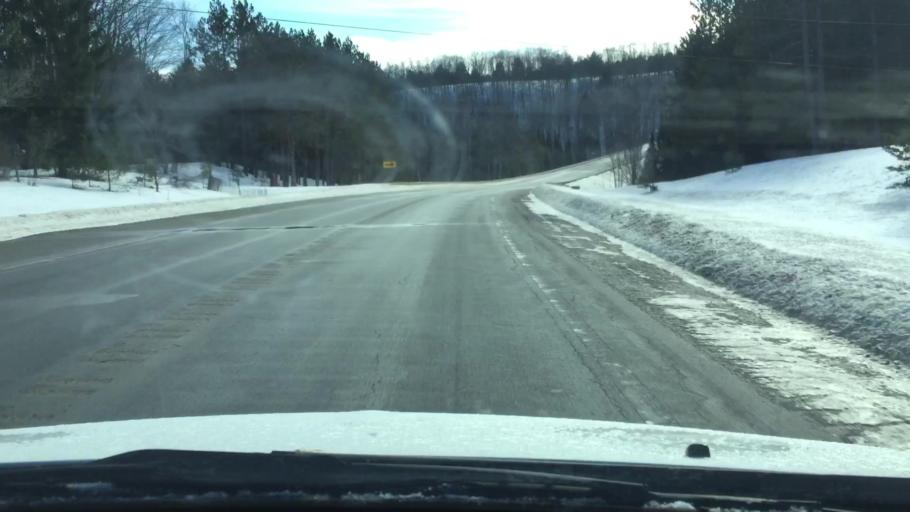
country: US
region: Michigan
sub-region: Antrim County
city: Mancelona
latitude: 44.9586
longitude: -85.0504
